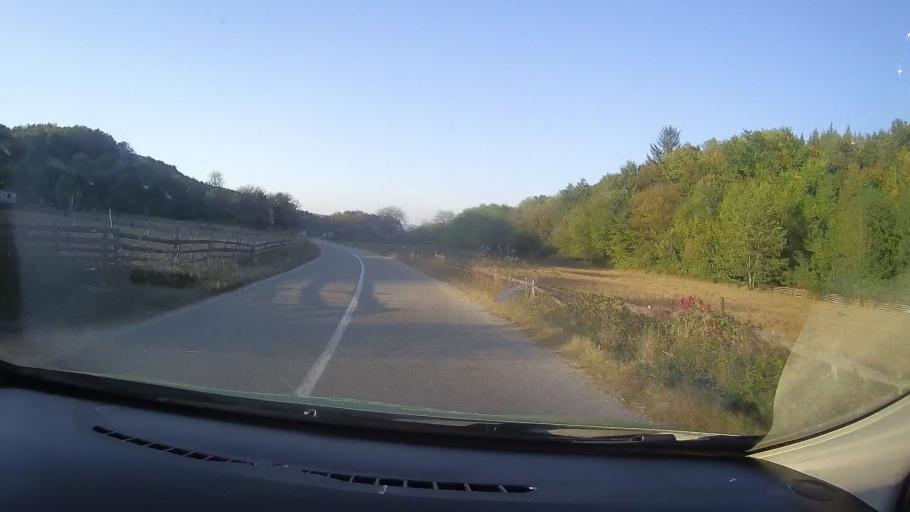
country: RO
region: Timis
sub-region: Comuna Fardea
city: Fardea
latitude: 45.7066
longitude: 22.1608
